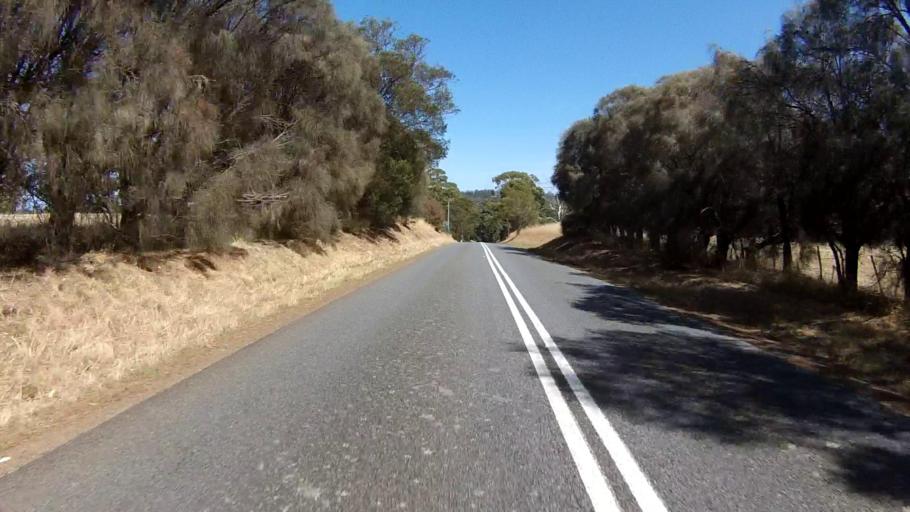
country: AU
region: Tasmania
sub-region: Sorell
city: Sorell
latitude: -42.2583
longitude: 148.0038
